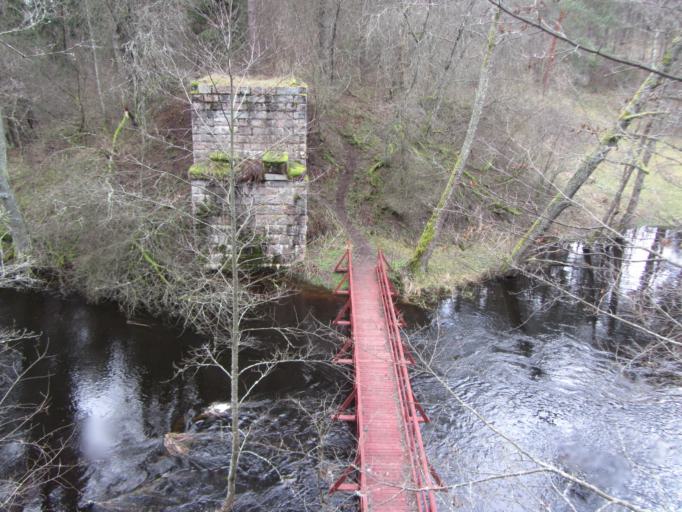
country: LT
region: Alytaus apskritis
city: Varena
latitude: 54.2876
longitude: 24.5432
